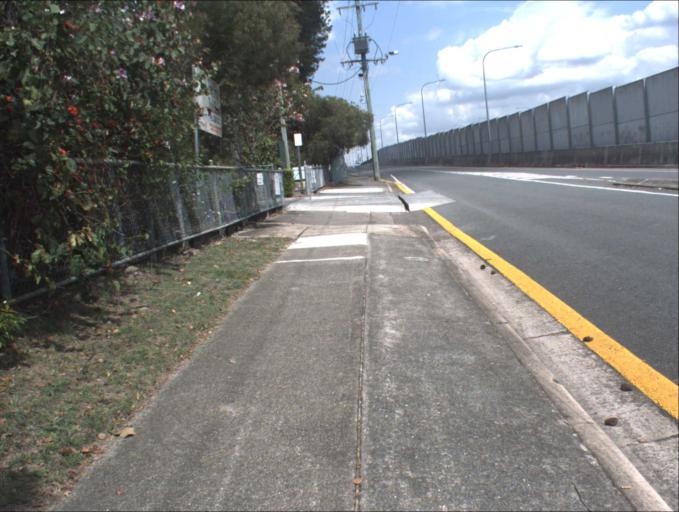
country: AU
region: Queensland
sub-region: Logan
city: Park Ridge South
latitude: -27.7013
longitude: 153.0389
